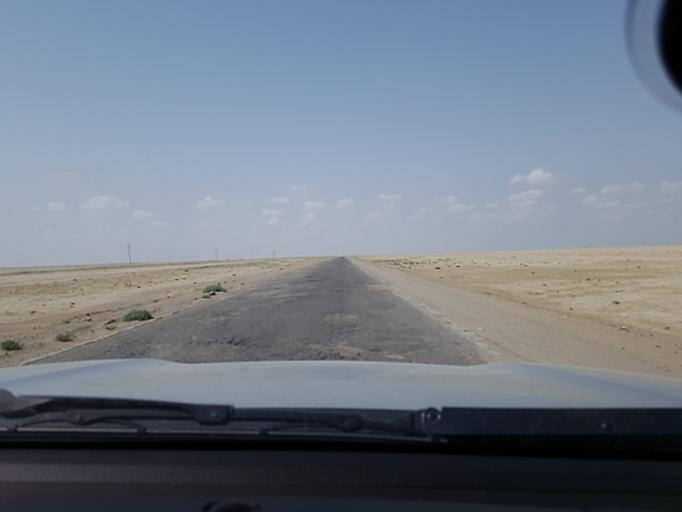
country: TM
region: Balkan
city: Gumdag
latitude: 38.6414
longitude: 54.3758
